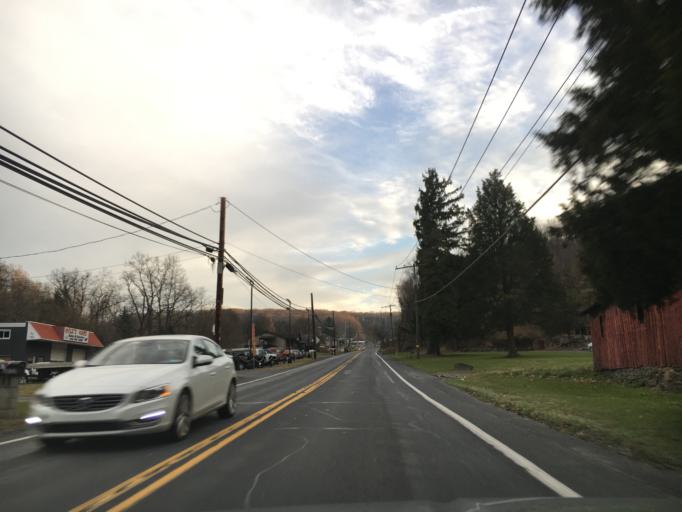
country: US
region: Pennsylvania
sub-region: Lehigh County
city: Slatington
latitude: 40.7279
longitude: -75.6177
